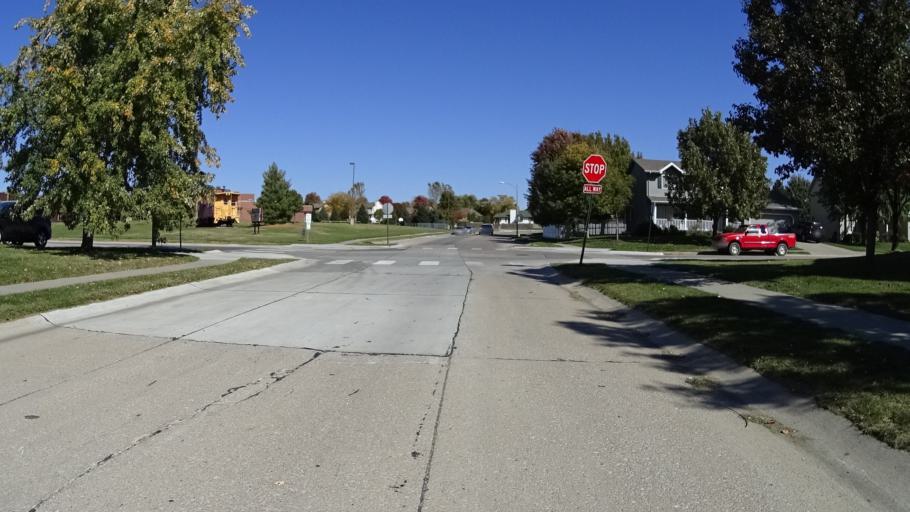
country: US
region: Nebraska
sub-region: Sarpy County
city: Papillion
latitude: 41.1546
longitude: -96.0114
